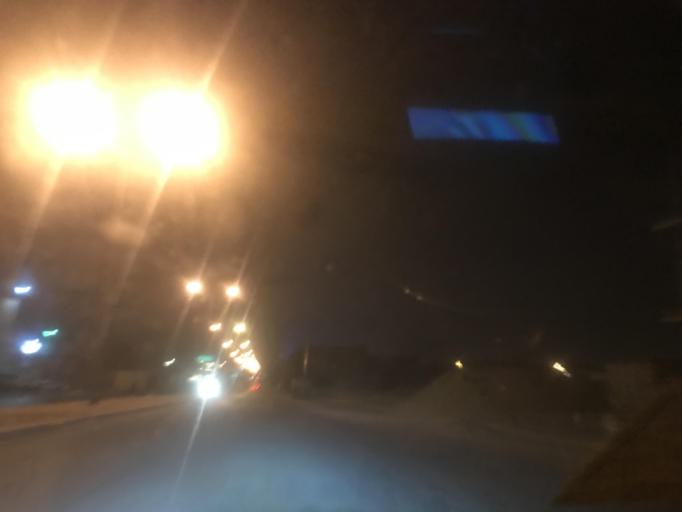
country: SA
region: Ar Riyad
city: Riyadh
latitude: 24.8073
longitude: 46.5900
